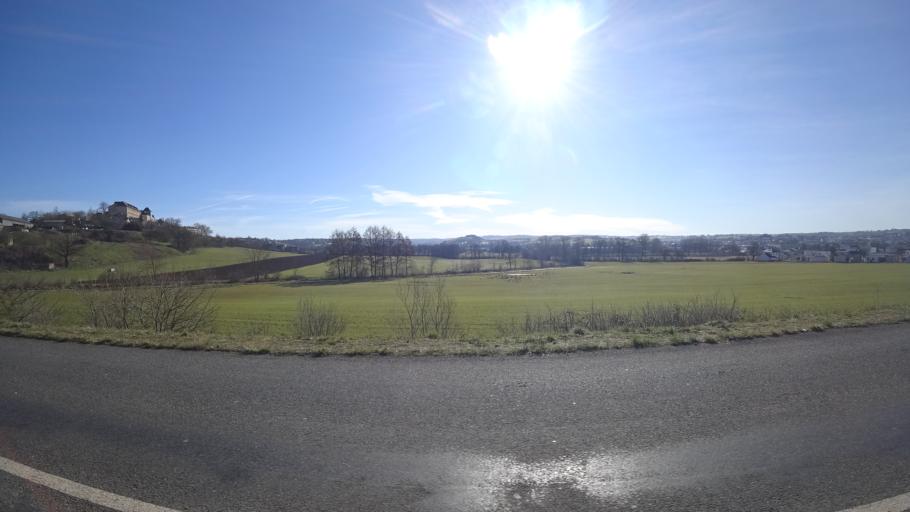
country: FR
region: Midi-Pyrenees
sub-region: Departement de l'Aveyron
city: Rodez
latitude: 44.3805
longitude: 2.5809
